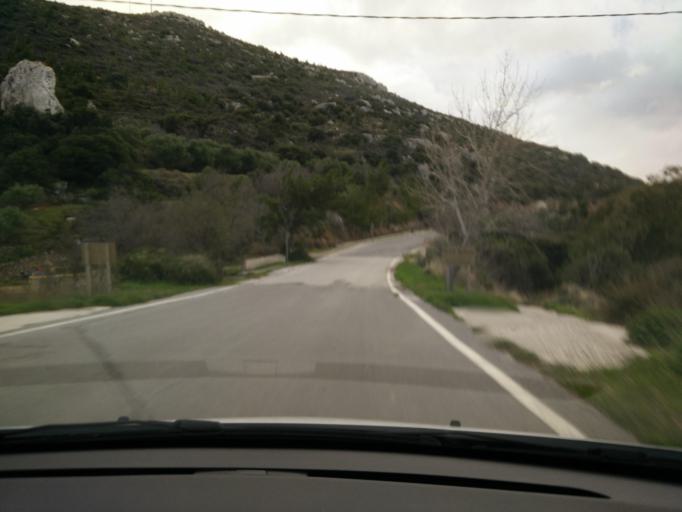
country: GR
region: Crete
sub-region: Nomos Lasithiou
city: Gra Liyia
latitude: 35.0813
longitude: 25.7105
